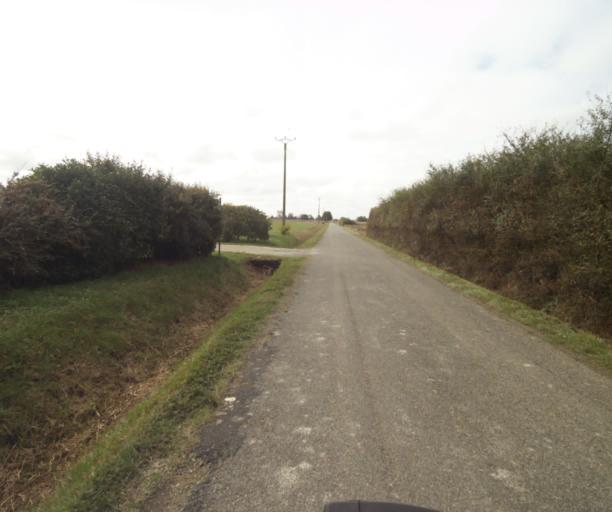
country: FR
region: Midi-Pyrenees
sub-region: Departement du Tarn-et-Garonne
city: Finhan
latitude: 43.9208
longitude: 1.2439
